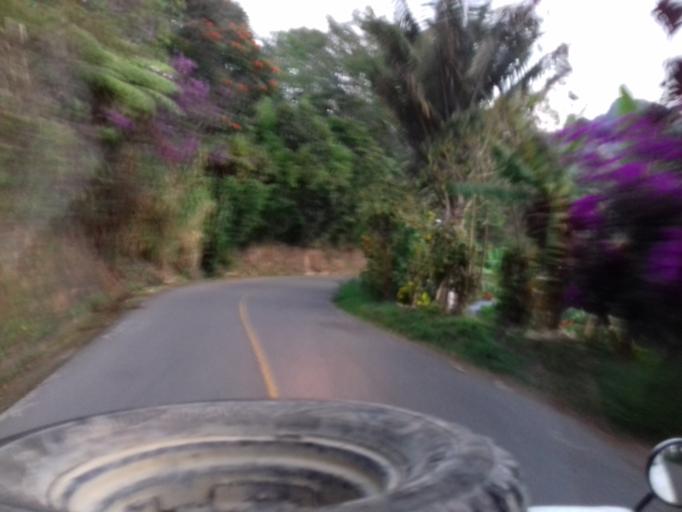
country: CO
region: Quindio
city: Salento
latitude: 4.6413
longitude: -75.5876
